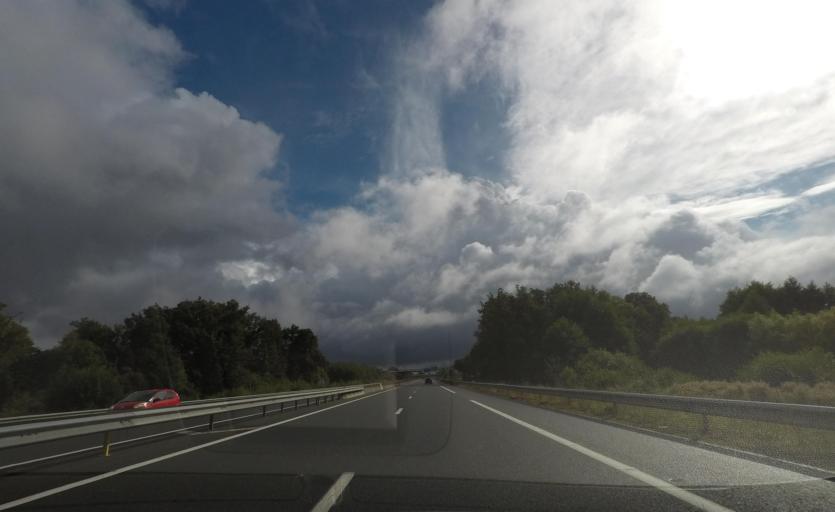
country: FR
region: Pays de la Loire
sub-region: Departement de la Vendee
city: La Ferriere
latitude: 46.6671
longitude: -1.3608
